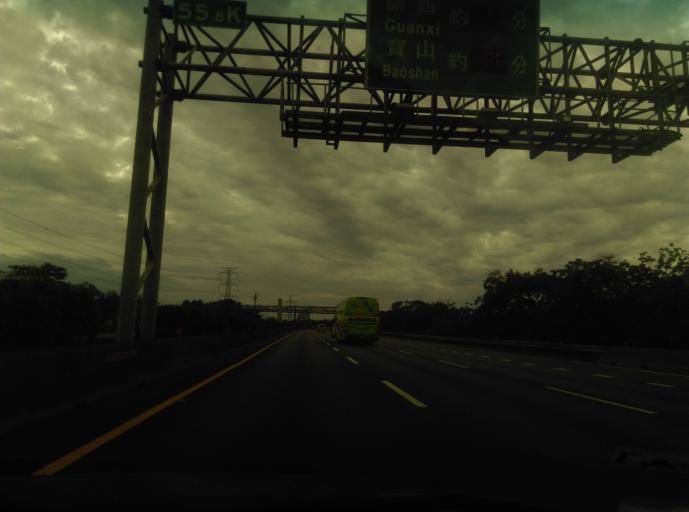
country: TW
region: Taiwan
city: Daxi
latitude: 24.9317
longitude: 121.3137
